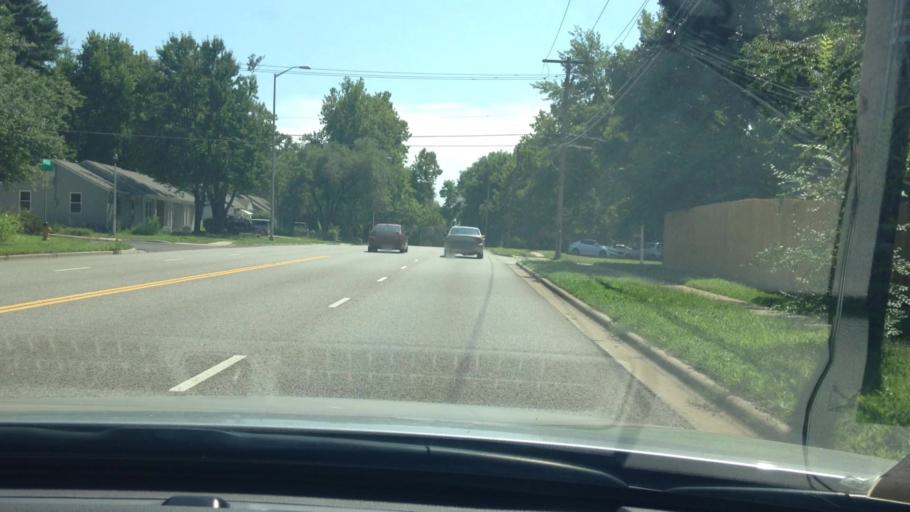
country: US
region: Kansas
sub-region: Johnson County
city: Overland Park
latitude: 38.9844
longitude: -94.6864
